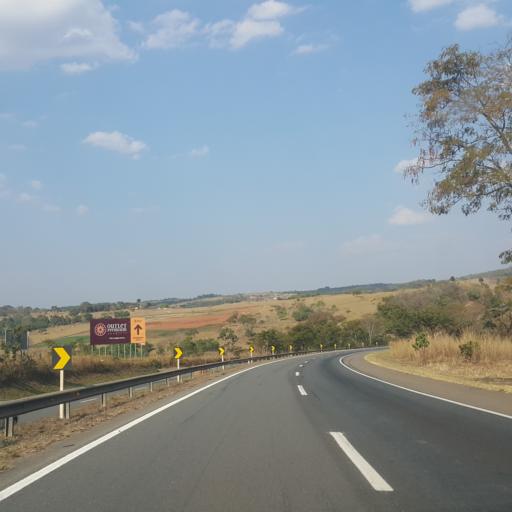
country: BR
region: Goias
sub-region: Abadiania
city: Abadiania
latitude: -16.1108
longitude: -48.5632
